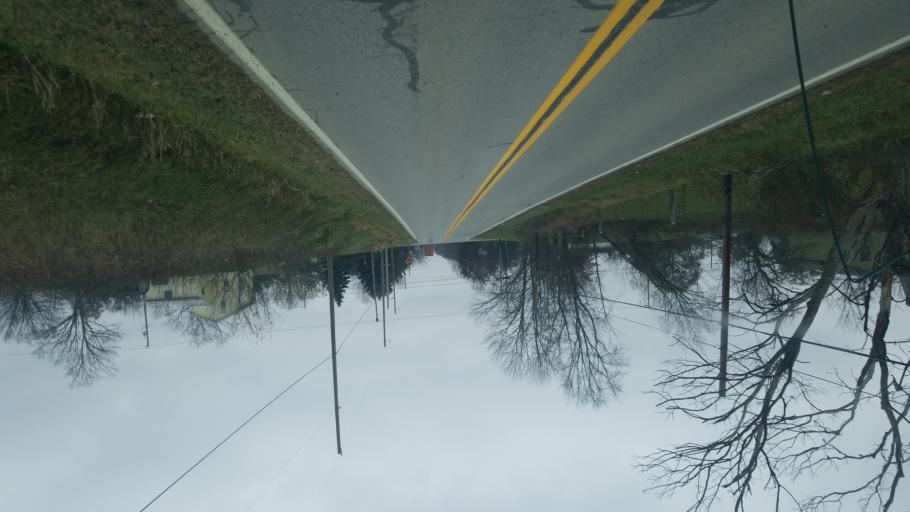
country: US
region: Ohio
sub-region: Medina County
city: Medina
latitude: 41.1359
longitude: -81.9250
